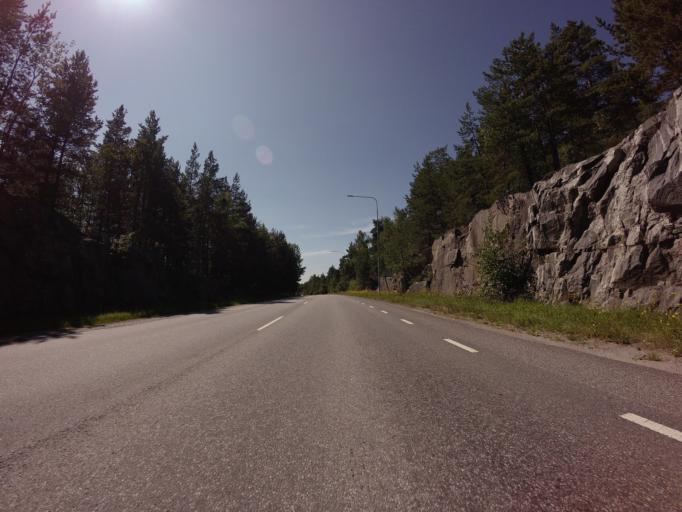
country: SE
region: Stockholm
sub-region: Lidingo
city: Brevik
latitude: 59.3477
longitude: 18.1968
